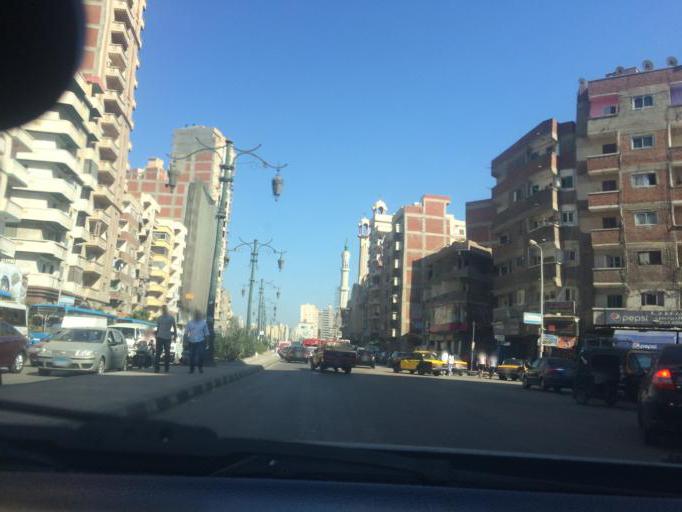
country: EG
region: Alexandria
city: Alexandria
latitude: 31.2611
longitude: 30.0103
